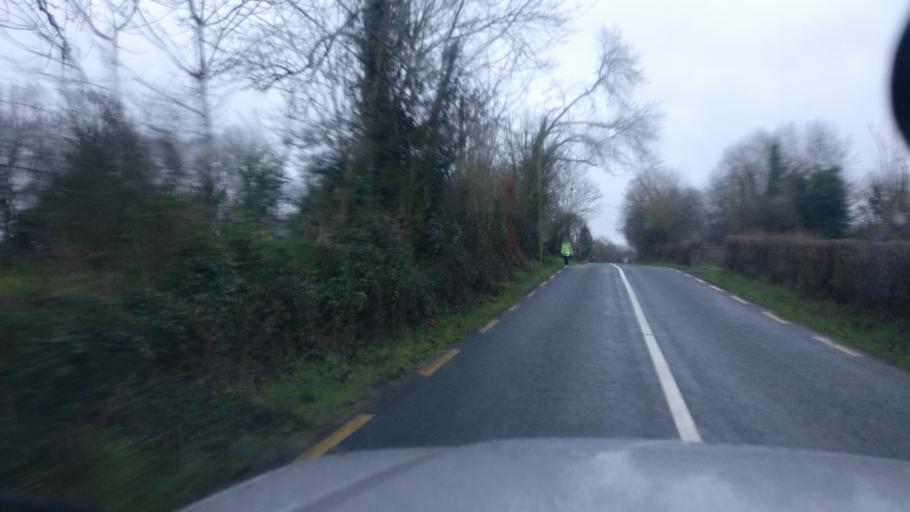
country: IE
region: Connaught
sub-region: County Galway
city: Ballinasloe
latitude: 53.2237
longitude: -8.1942
